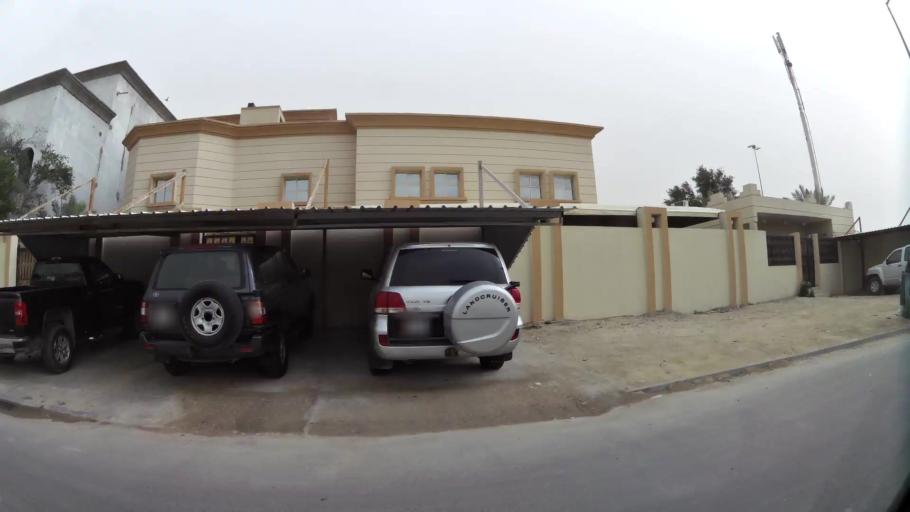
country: QA
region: Baladiyat ad Dawhah
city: Doha
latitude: 25.2417
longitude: 51.5181
